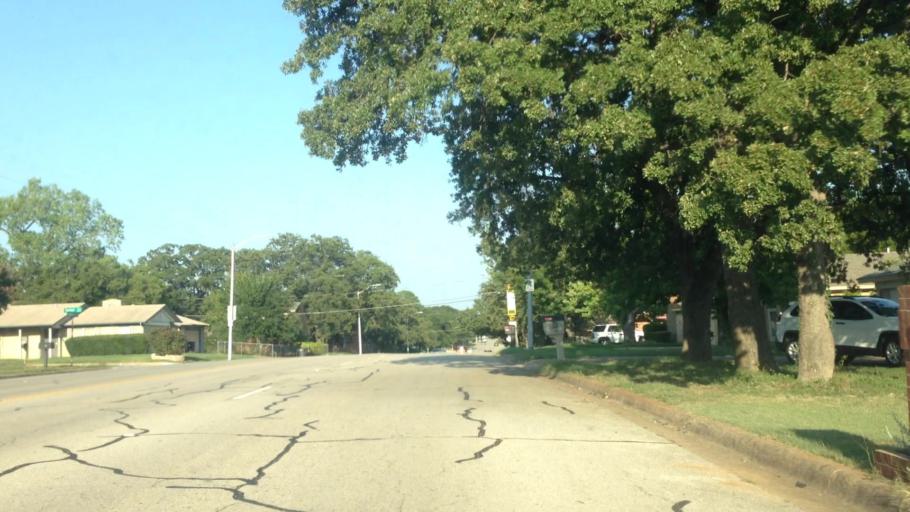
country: US
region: Texas
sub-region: Tarrant County
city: Richland Hills
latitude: 32.7543
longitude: -97.2098
